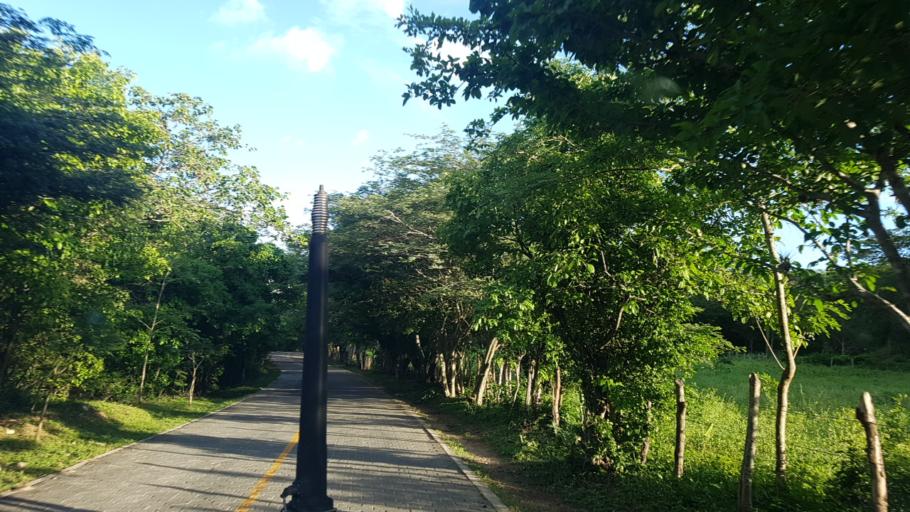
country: NI
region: Nueva Segovia
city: Ocotal
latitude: 13.6418
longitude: -86.5921
